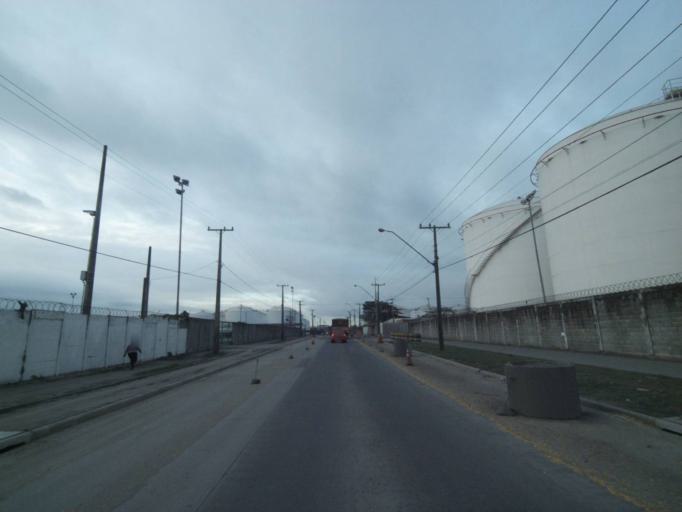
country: BR
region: Parana
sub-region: Paranagua
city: Paranagua
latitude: -25.5124
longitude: -48.5340
